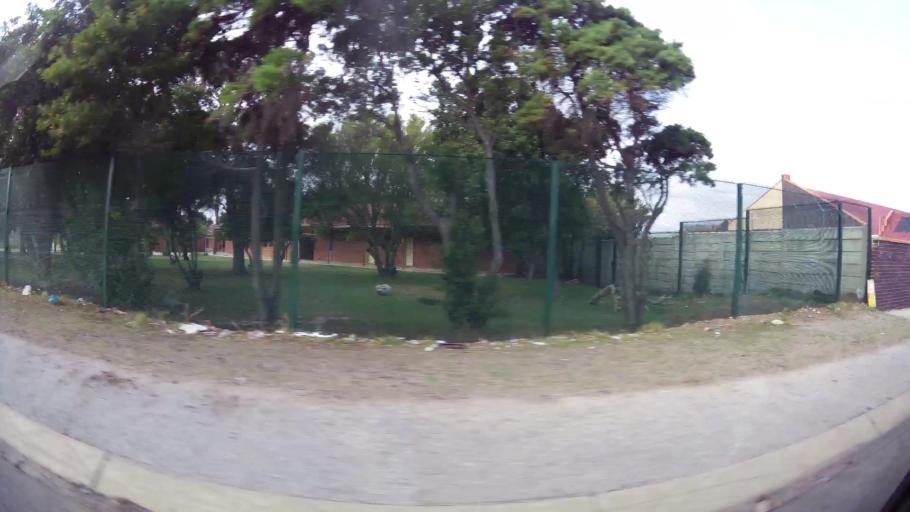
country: ZA
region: Eastern Cape
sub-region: Nelson Mandela Bay Metropolitan Municipality
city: Port Elizabeth
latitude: -33.9210
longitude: 25.5340
